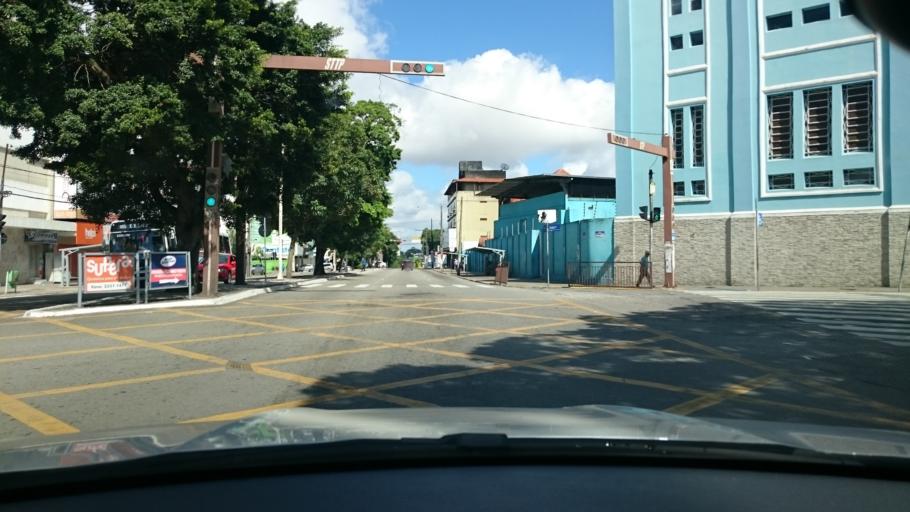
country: BR
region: Paraiba
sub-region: Campina Grande
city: Campina Grande
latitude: -7.2199
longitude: -35.8850
